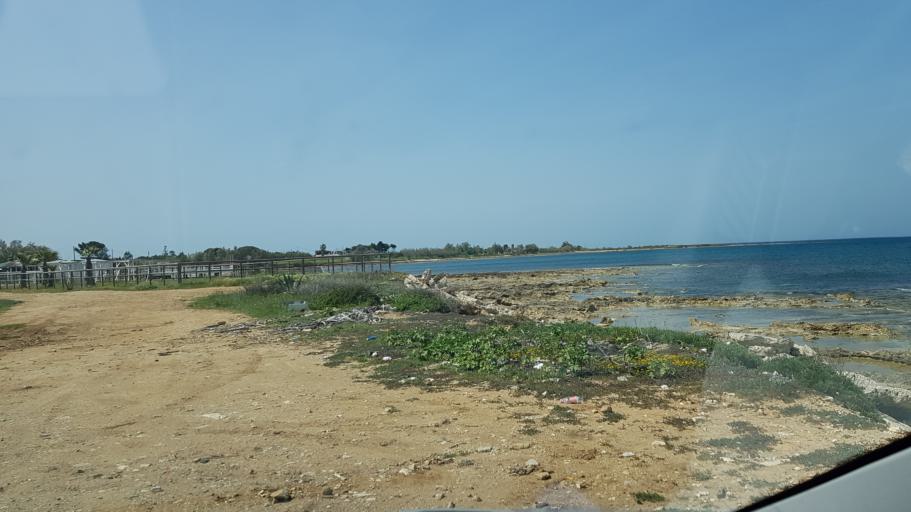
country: IT
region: Apulia
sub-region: Provincia di Brindisi
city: Materdomini
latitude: 40.6684
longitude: 17.9495
